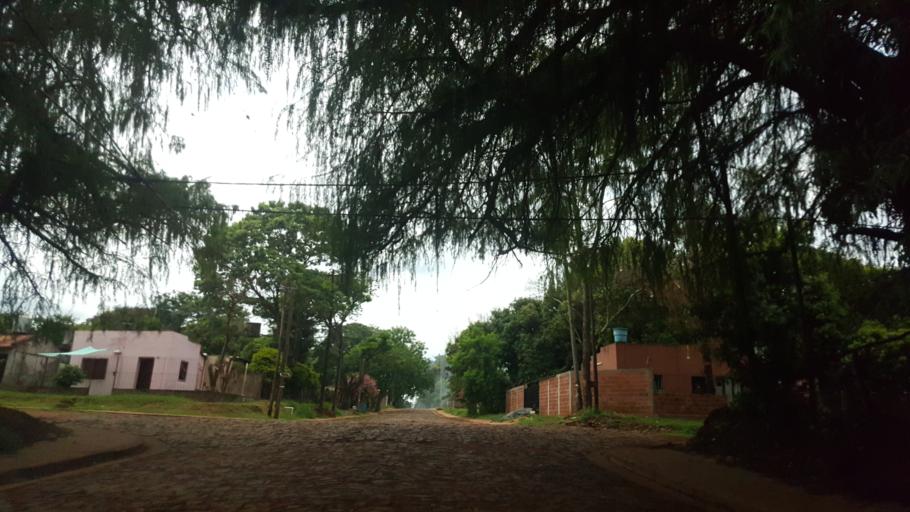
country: AR
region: Misiones
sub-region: Departamento de Capital
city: Posadas
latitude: -27.4294
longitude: -55.8891
